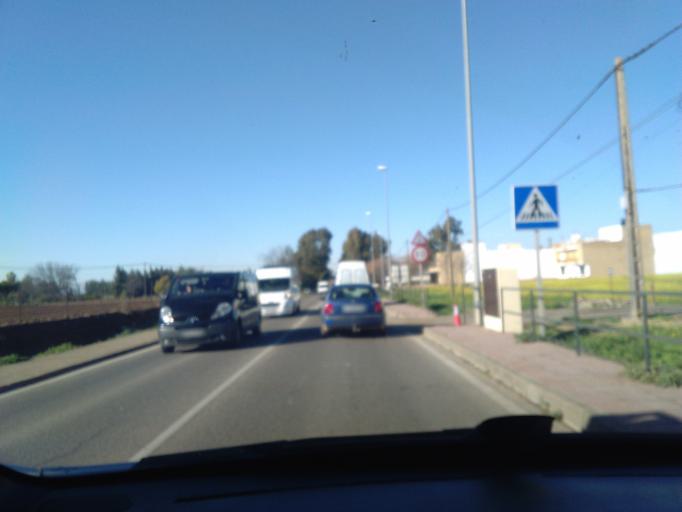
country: ES
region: Andalusia
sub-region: Provincia de Sevilla
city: Sevilla
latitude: 37.4280
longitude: -5.9304
